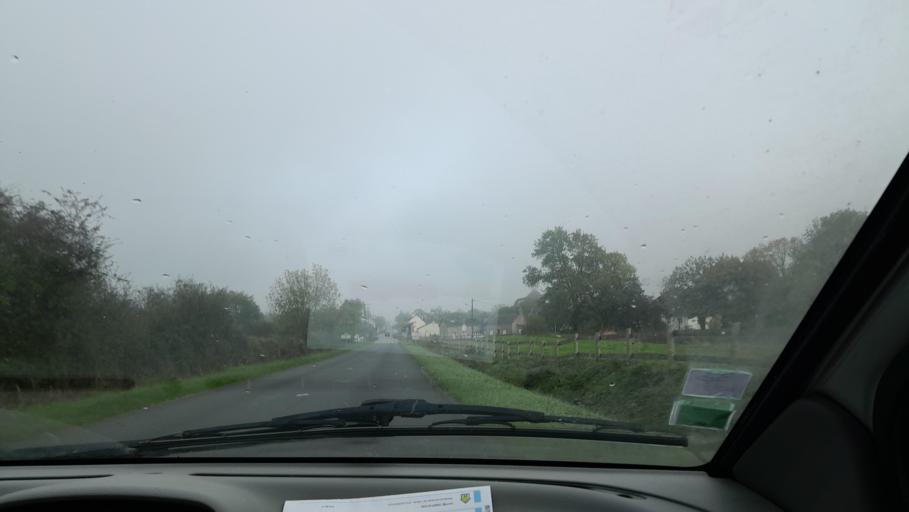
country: FR
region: Pays de la Loire
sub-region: Departement de la Mayenne
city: Saint-Pierre-la-Cour
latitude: 48.1033
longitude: -1.0209
